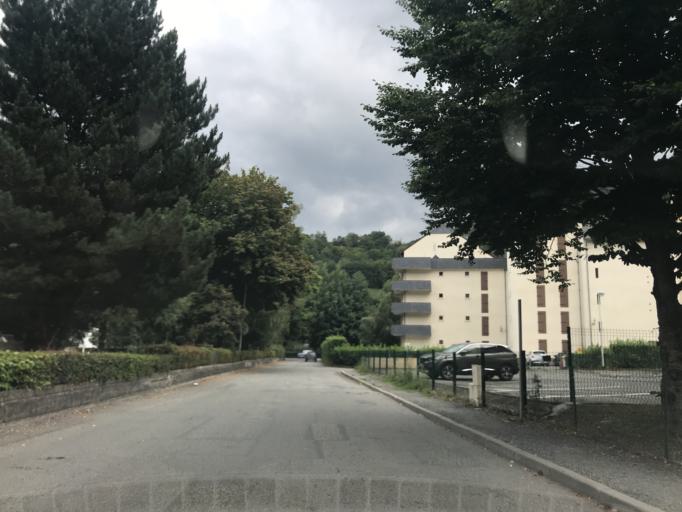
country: FR
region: Midi-Pyrenees
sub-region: Departement des Hautes-Pyrenees
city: Saint-Lary-Soulan
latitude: 42.8211
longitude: 0.3255
